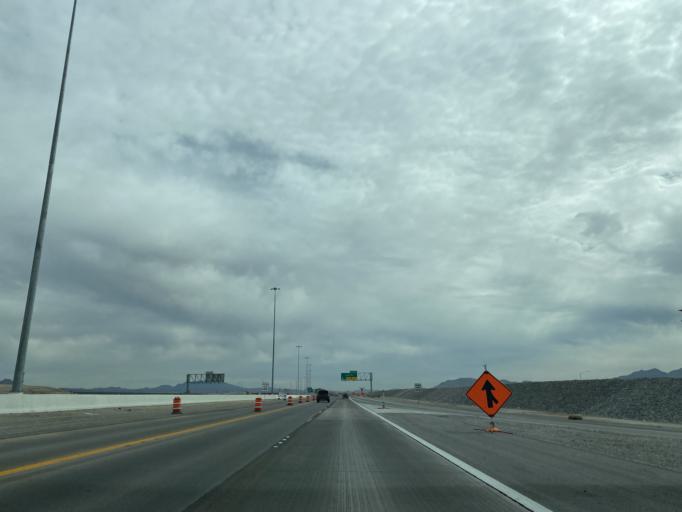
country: US
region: Nevada
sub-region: Clark County
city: Nellis Air Force Base
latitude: 36.2907
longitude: -115.1317
